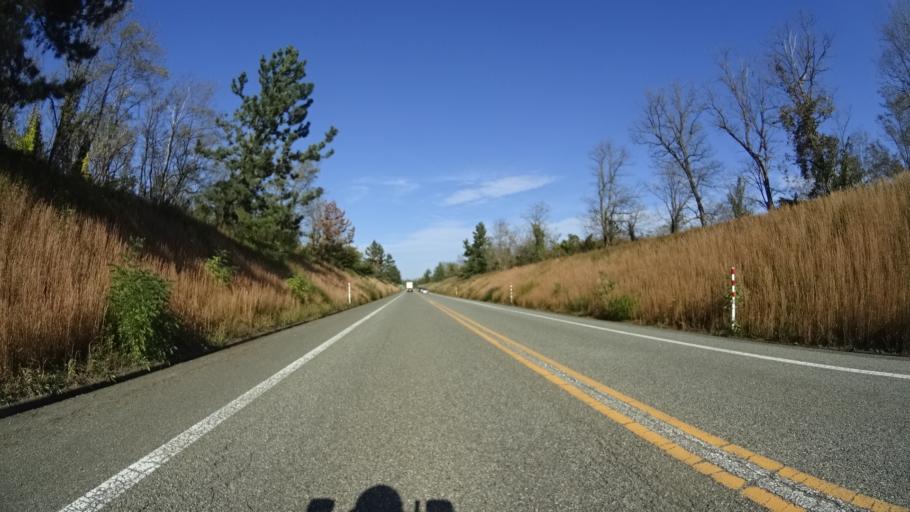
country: JP
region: Ishikawa
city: Kanazawa-shi
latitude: 36.6418
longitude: 136.6333
